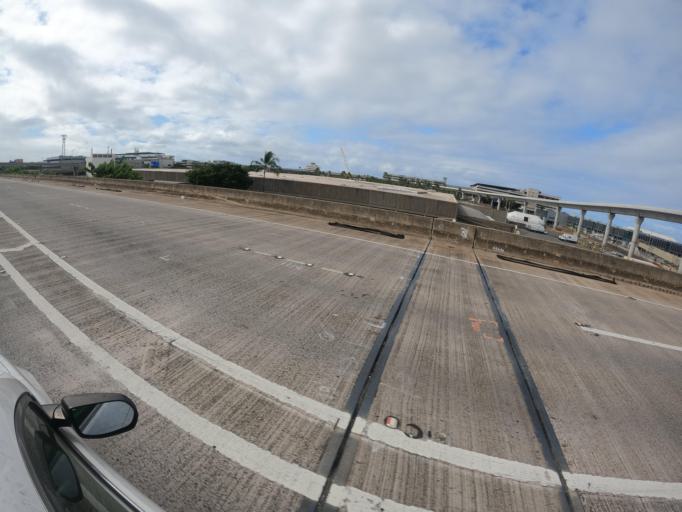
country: US
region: Hawaii
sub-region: Honolulu County
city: Hickam Field
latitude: 21.3380
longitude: -157.9217
